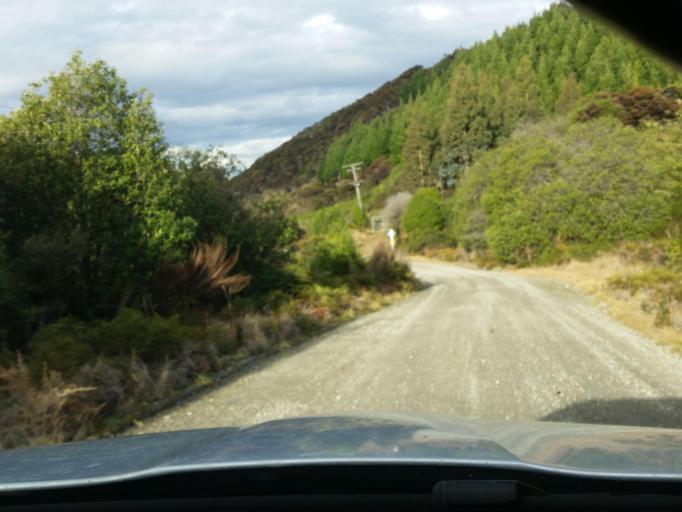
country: NZ
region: Southland
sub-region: Southland District
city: Te Anau
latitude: -45.7948
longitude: 167.6279
